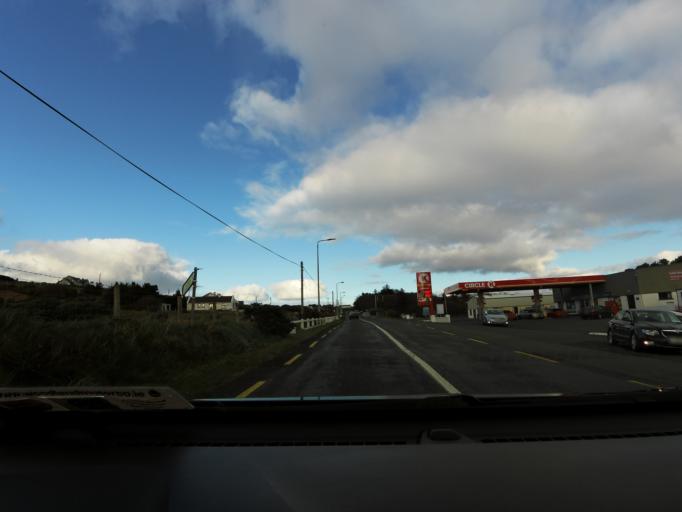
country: IE
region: Connaught
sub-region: Maigh Eo
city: Belmullet
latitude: 53.9524
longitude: -9.9719
